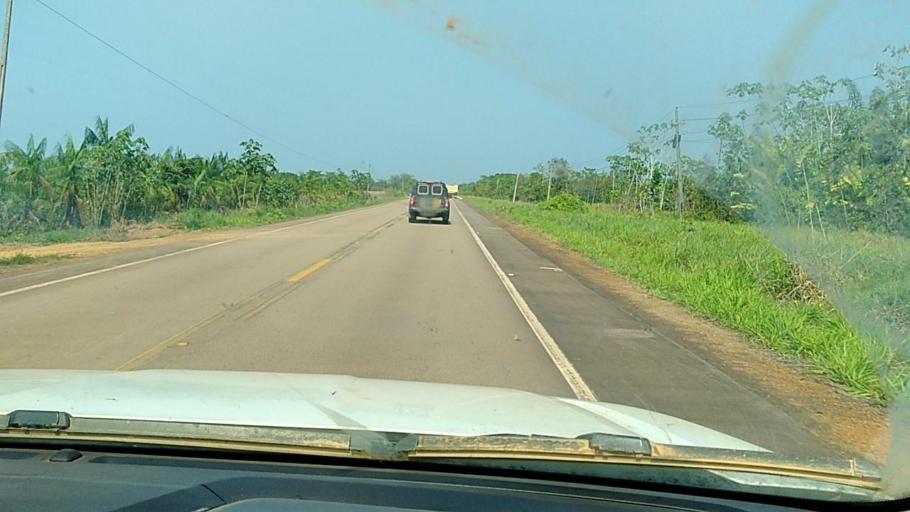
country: BR
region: Amazonas
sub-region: Humaita
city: Humaita
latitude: -7.5778
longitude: -63.1236
